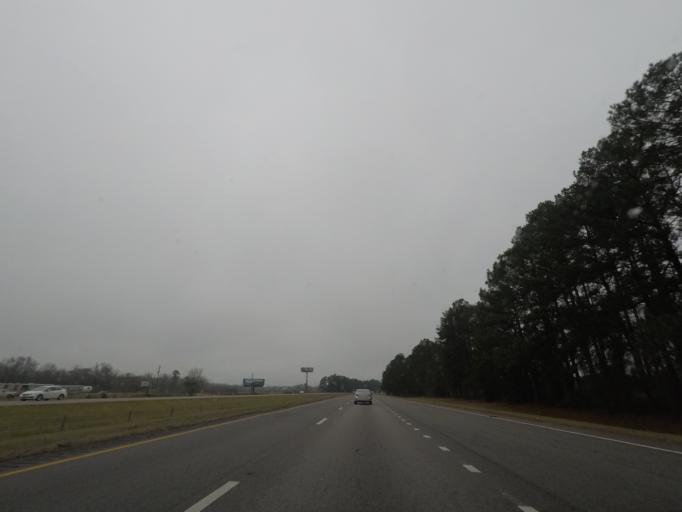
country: US
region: South Carolina
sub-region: Florence County
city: Timmonsville
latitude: 33.9649
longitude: -80.0438
